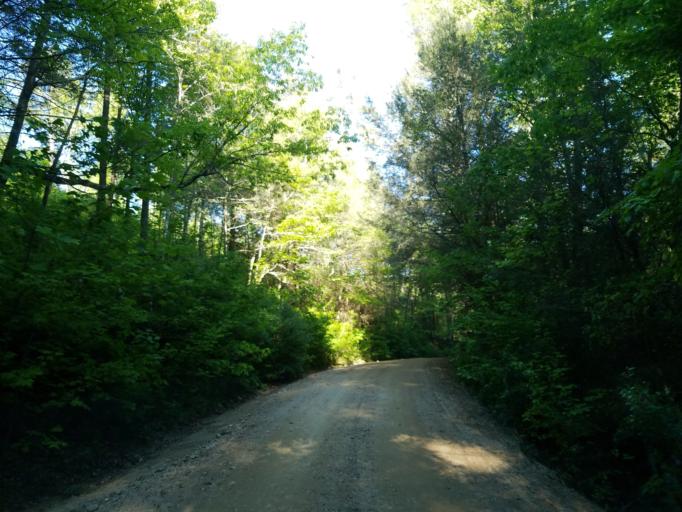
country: US
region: Georgia
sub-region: Lumpkin County
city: Dahlonega
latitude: 34.6998
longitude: -84.1449
